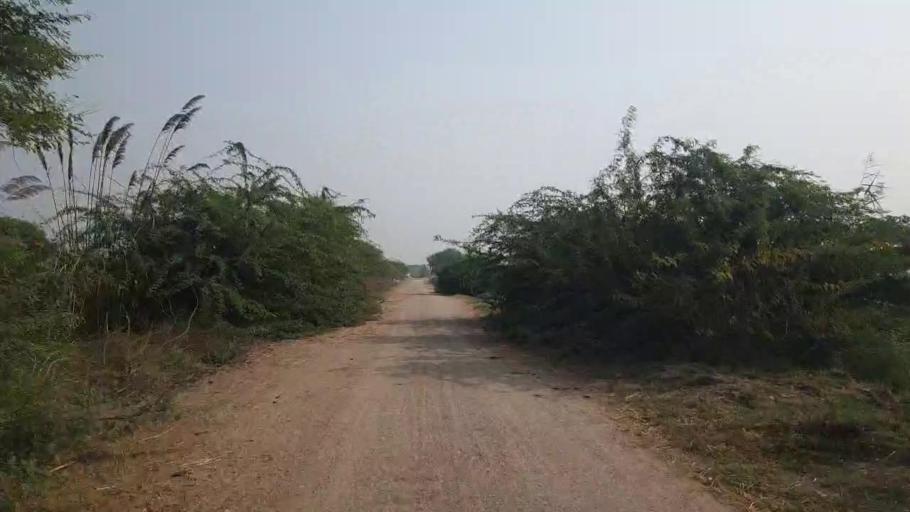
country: PK
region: Sindh
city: Tando Muhammad Khan
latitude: 25.2690
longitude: 68.5069
